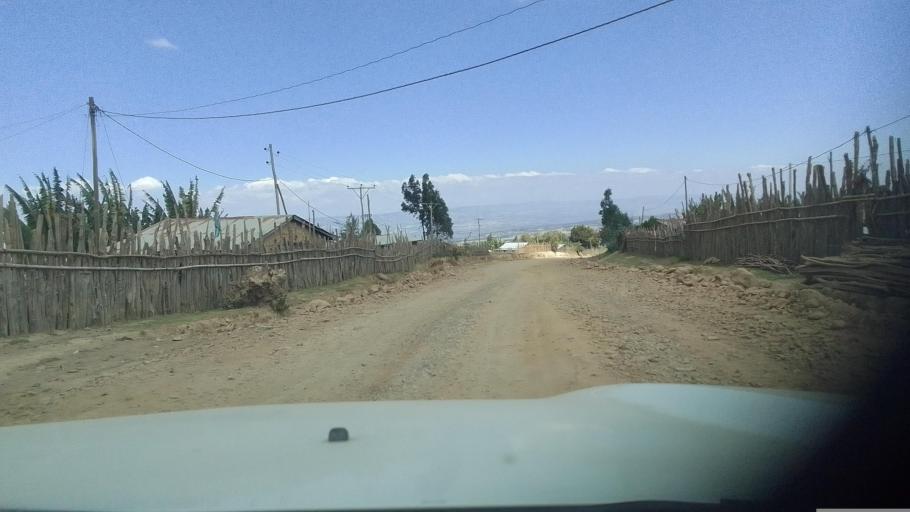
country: ET
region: Oromiya
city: Hagere Hiywet
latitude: 8.8455
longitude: 37.8862
